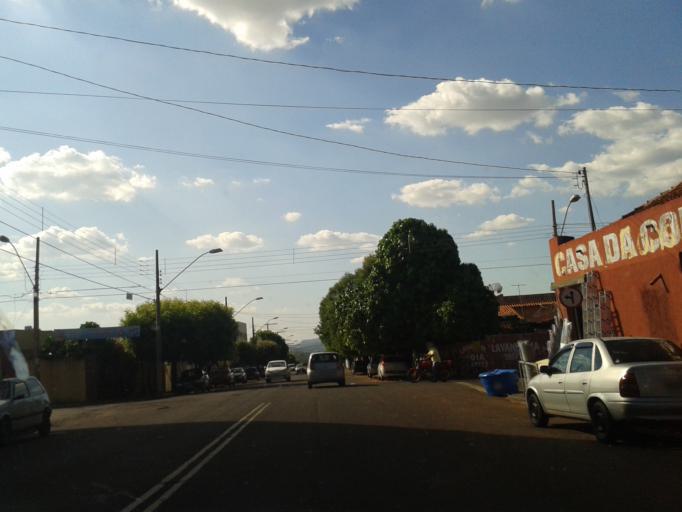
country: BR
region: Minas Gerais
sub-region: Ituiutaba
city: Ituiutaba
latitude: -18.9801
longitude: -49.4574
